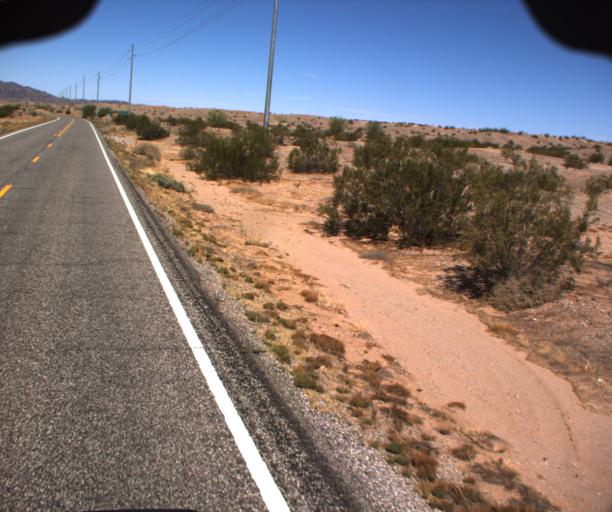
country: US
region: Arizona
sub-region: La Paz County
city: Parker
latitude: 33.9958
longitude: -114.1832
